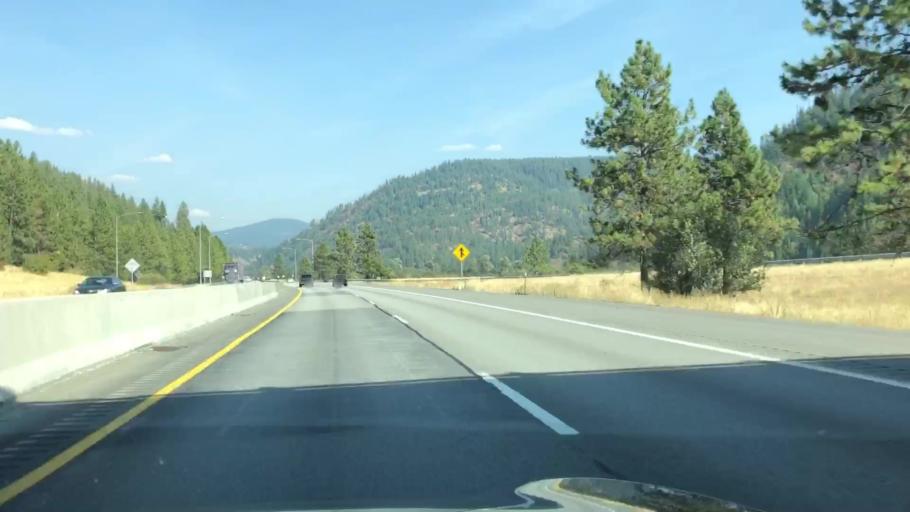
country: US
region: Idaho
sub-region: Kootenai County
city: Coeur d'Alene
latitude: 47.6237
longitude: -116.6487
